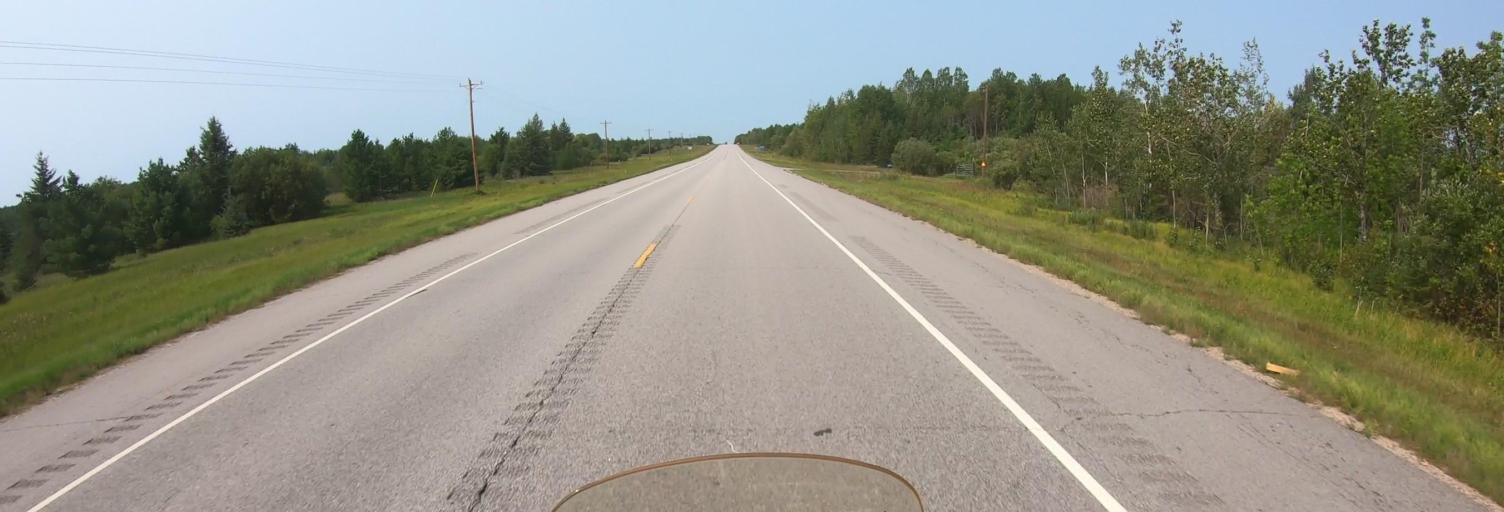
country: CA
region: Ontario
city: Fort Frances
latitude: 48.4101
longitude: -93.1496
